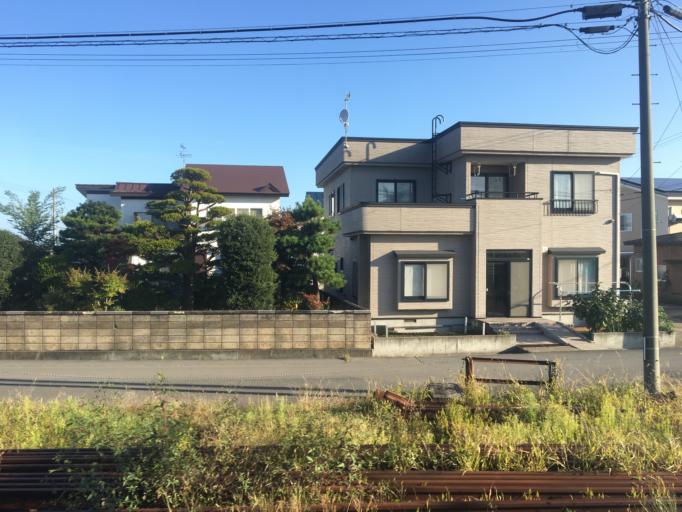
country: JP
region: Aomori
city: Hirosaki
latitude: 40.5875
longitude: 140.5197
